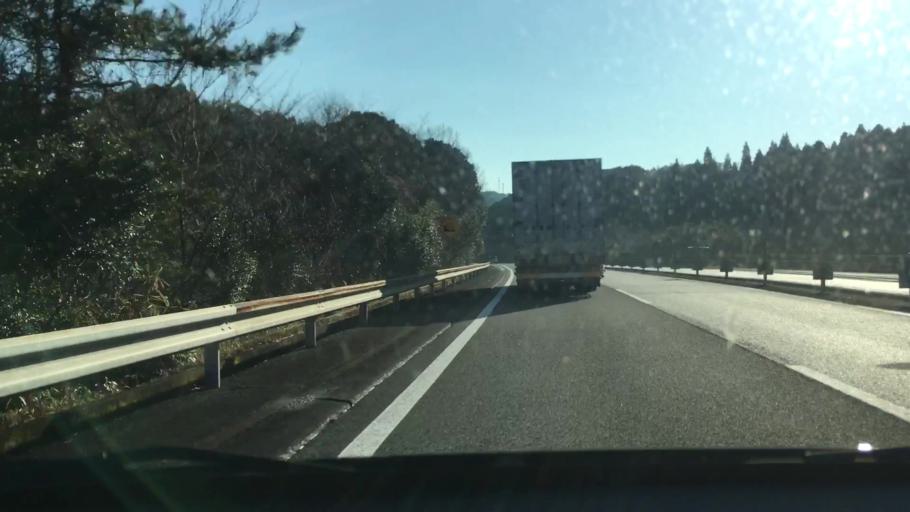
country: JP
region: Kagoshima
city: Kajiki
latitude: 31.8895
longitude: 130.6973
